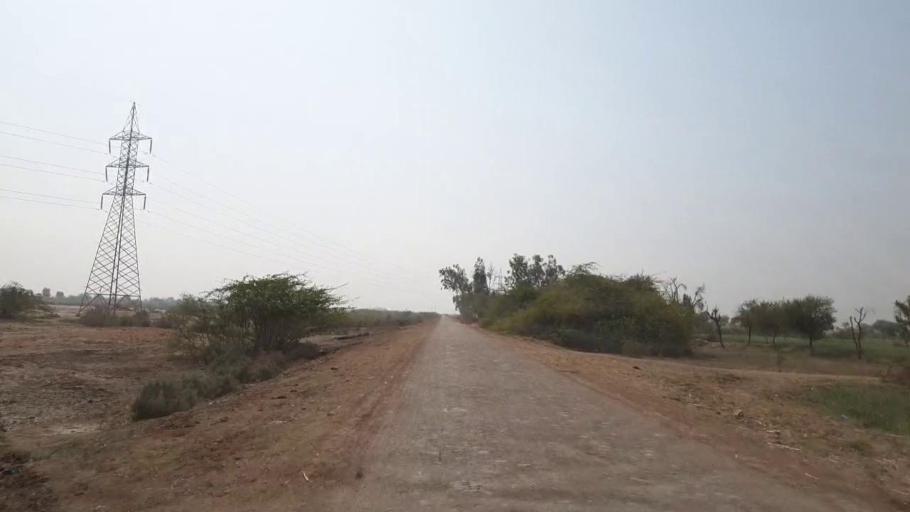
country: PK
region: Sindh
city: Mirpur Khas
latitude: 25.5945
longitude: 69.0250
